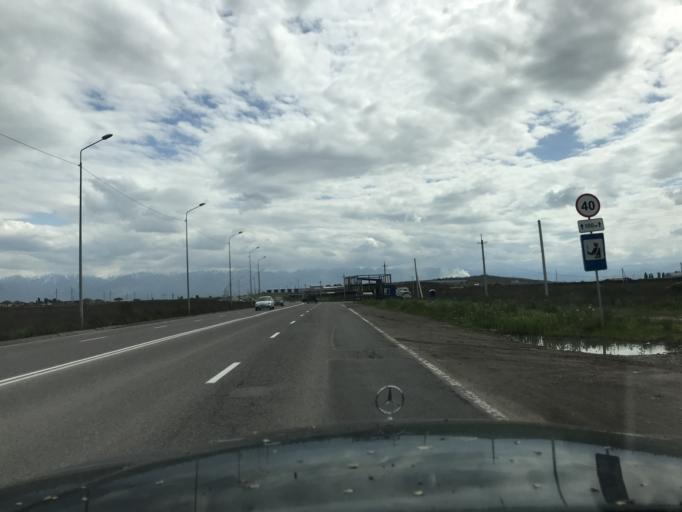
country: KZ
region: Almaty Oblysy
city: Burunday
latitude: 43.3502
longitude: 76.8340
